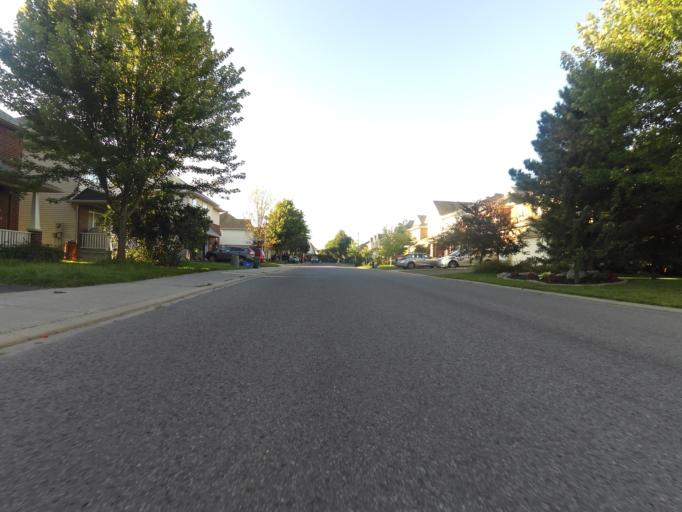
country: CA
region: Ontario
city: Ottawa
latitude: 45.2887
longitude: -75.7072
